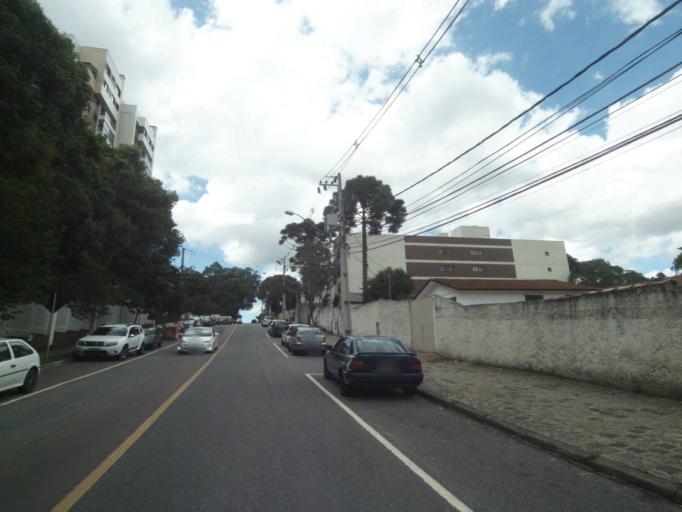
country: BR
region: Parana
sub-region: Curitiba
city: Curitiba
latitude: -25.4349
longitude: -49.3254
